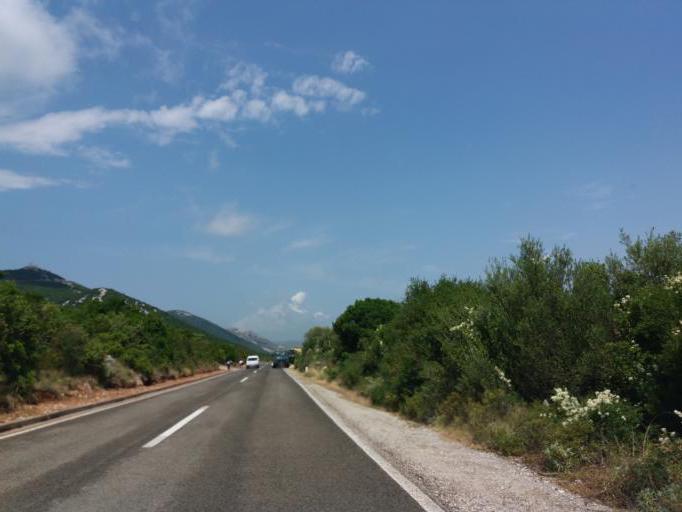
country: HR
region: Zadarska
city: Sali
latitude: 43.9834
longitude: 15.0745
